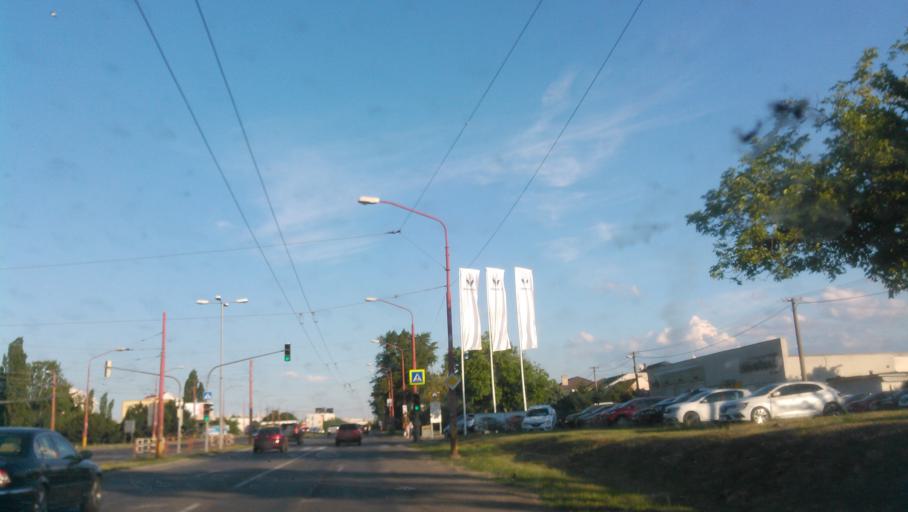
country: SK
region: Bratislavsky
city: Bratislava
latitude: 48.1432
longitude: 17.1900
